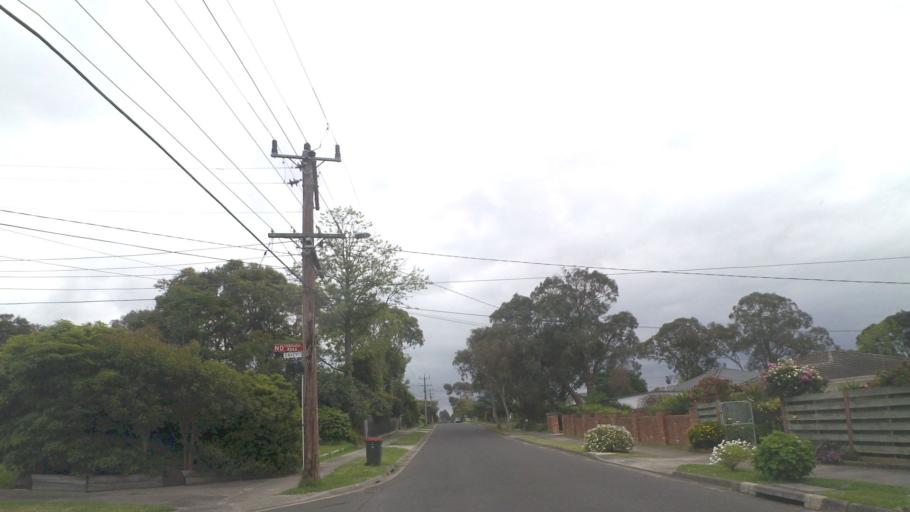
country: AU
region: Victoria
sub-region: Knox
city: Bayswater
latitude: -37.8568
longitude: 145.2709
